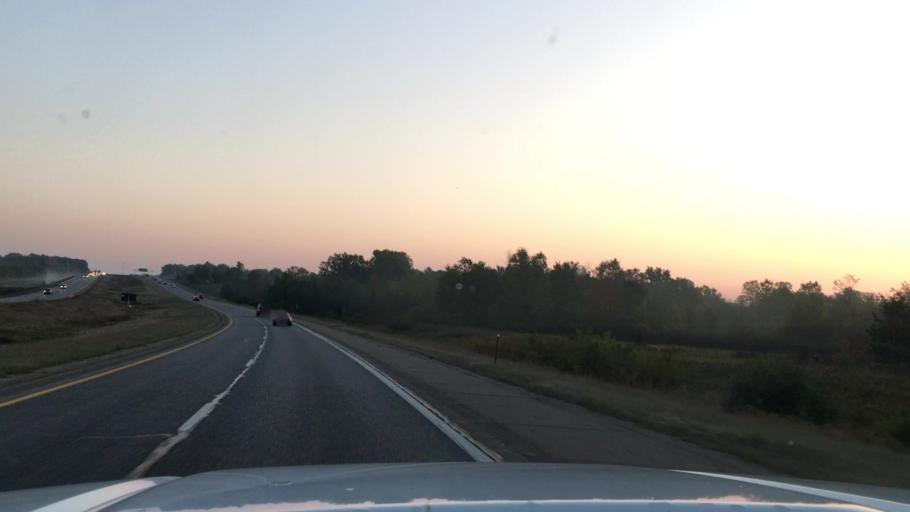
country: US
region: Michigan
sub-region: Kent County
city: Caledonia
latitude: 42.8590
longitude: -85.5050
